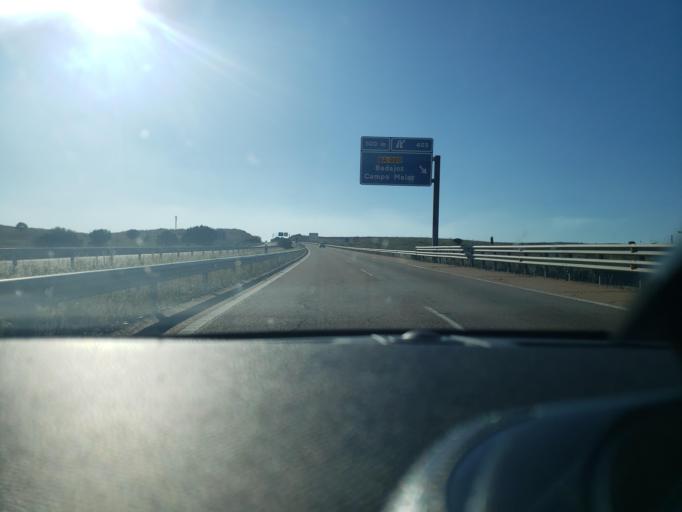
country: ES
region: Extremadura
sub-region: Provincia de Badajoz
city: Badajoz
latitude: 38.9145
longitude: -6.9878
